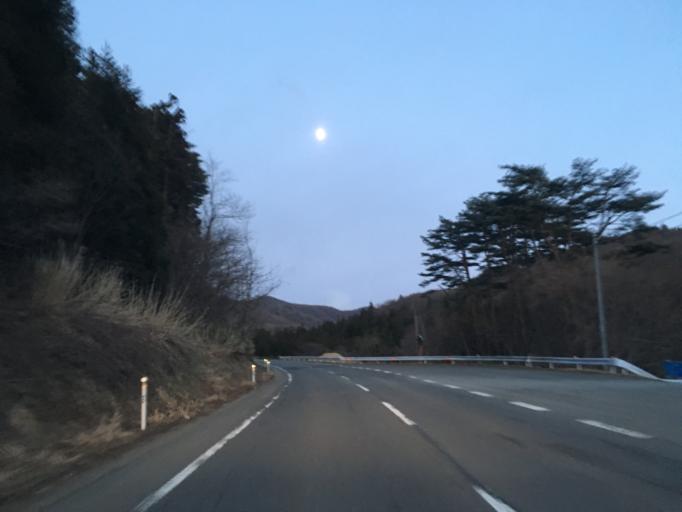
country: JP
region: Fukushima
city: Inawashiro
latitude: 37.3950
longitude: 140.1696
